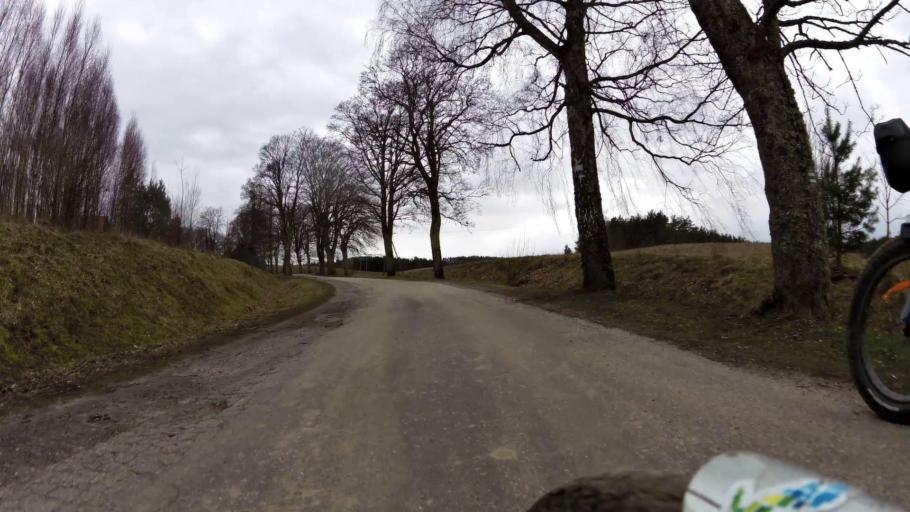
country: PL
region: Pomeranian Voivodeship
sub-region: Powiat bytowski
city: Trzebielino
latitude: 54.1045
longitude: 17.1299
